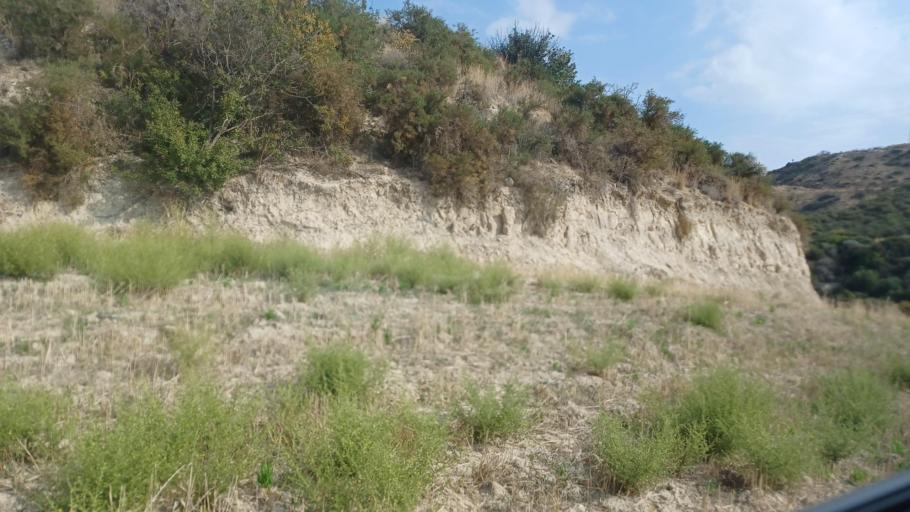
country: CY
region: Pafos
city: Polis
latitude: 34.9713
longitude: 32.4567
